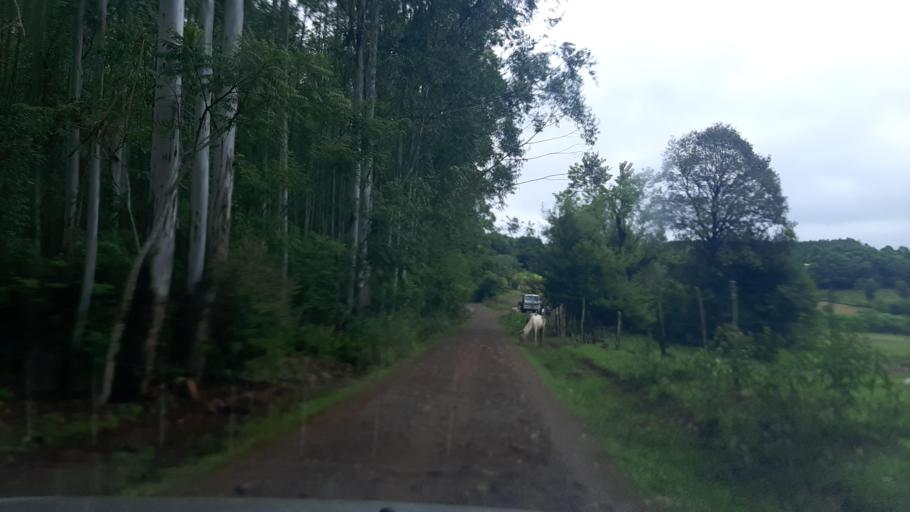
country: BR
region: Parana
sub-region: Ampere
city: Ampere
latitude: -26.0569
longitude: -53.5461
